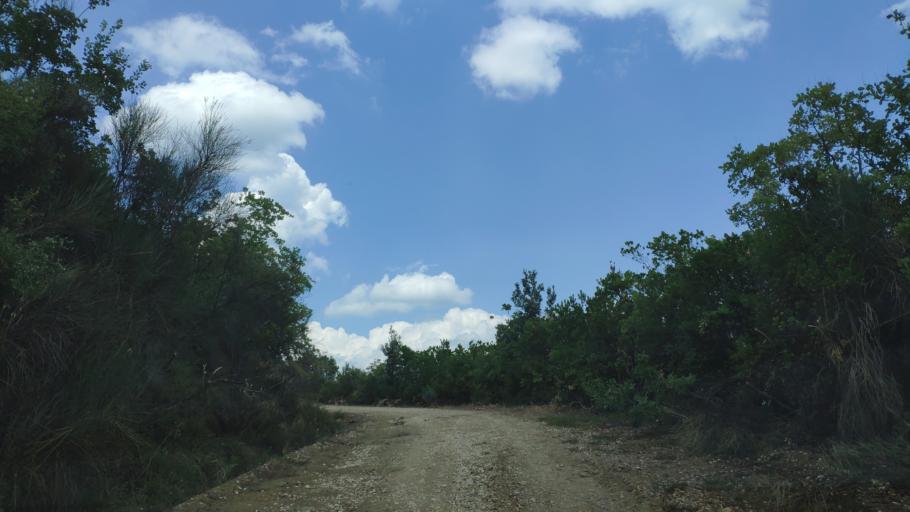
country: GR
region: Epirus
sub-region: Nomos Artas
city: Agios Dimitrios
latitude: 39.3137
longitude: 21.0183
